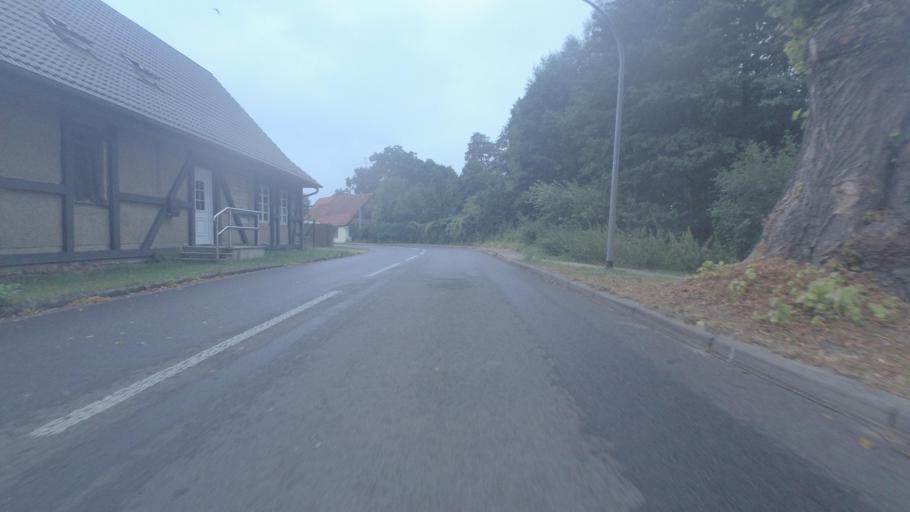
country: DE
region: Brandenburg
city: Heiligengrabe
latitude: 53.1401
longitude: 12.3475
